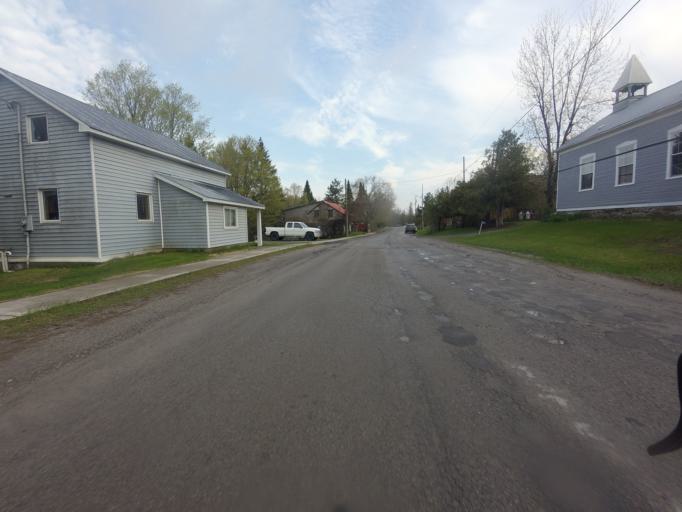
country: CA
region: Ontario
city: Carleton Place
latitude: 45.1931
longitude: -76.3262
